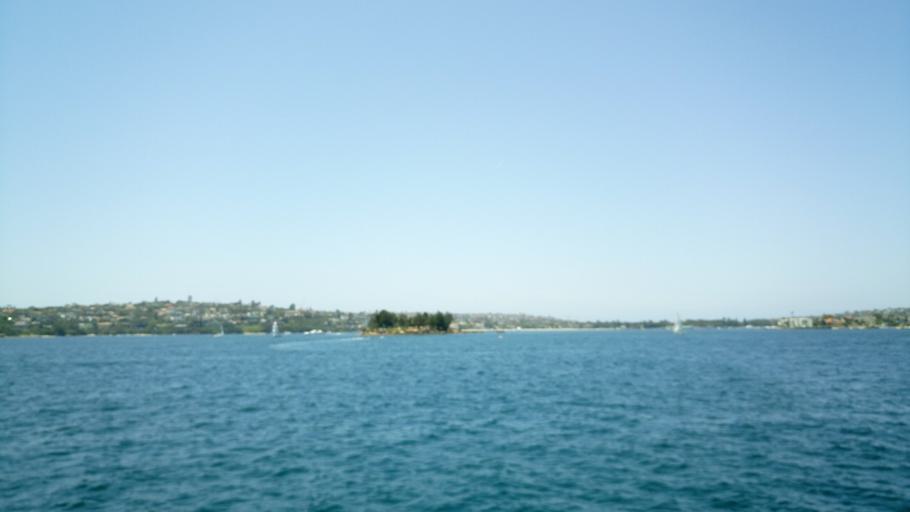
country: AU
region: New South Wales
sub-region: Woollahra
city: Point Piper
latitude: -33.8537
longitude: 151.2506
